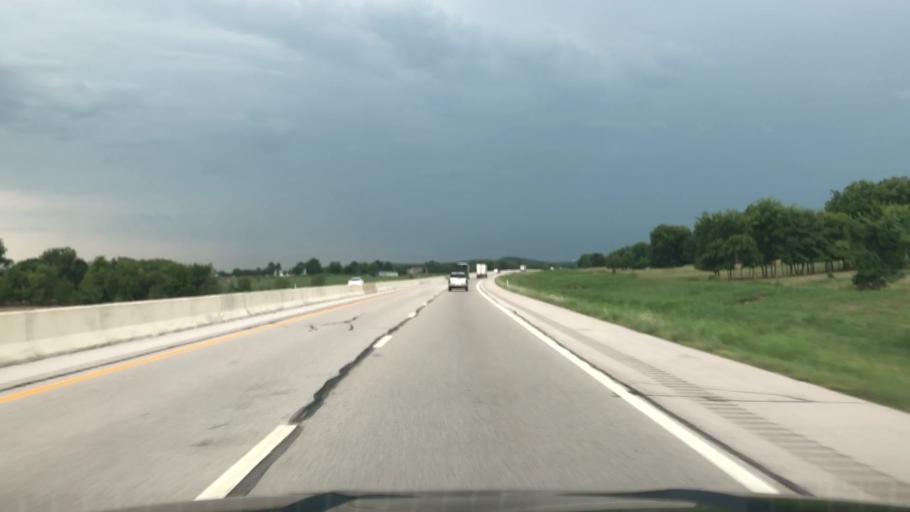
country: US
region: Oklahoma
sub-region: Rogers County
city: Bushyhead
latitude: 36.3566
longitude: -95.4573
